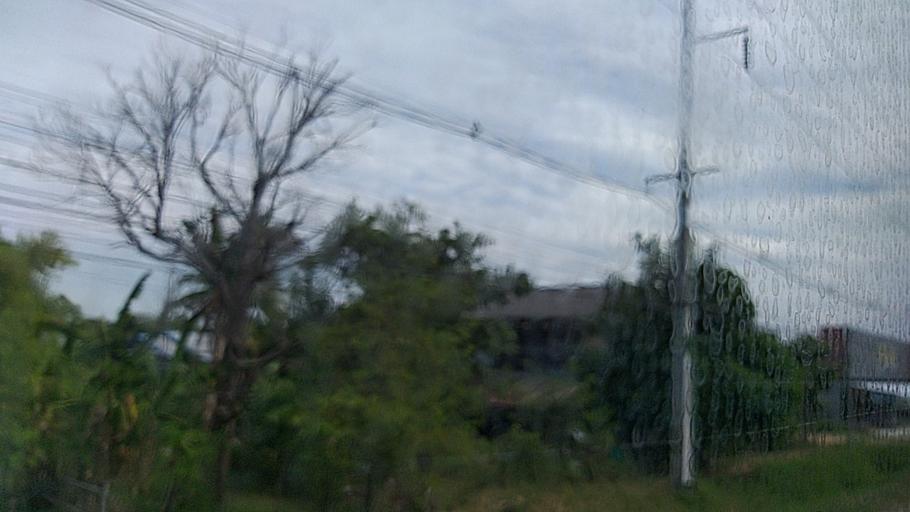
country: TH
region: Maha Sarakham
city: Chiang Yuen
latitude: 16.4182
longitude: 103.0793
